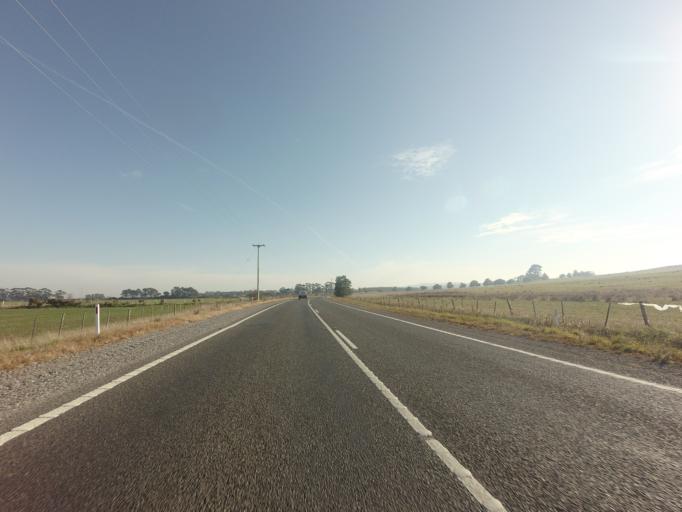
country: AU
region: Tasmania
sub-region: Northern Midlands
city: Longford
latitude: -41.5562
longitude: 147.0639
